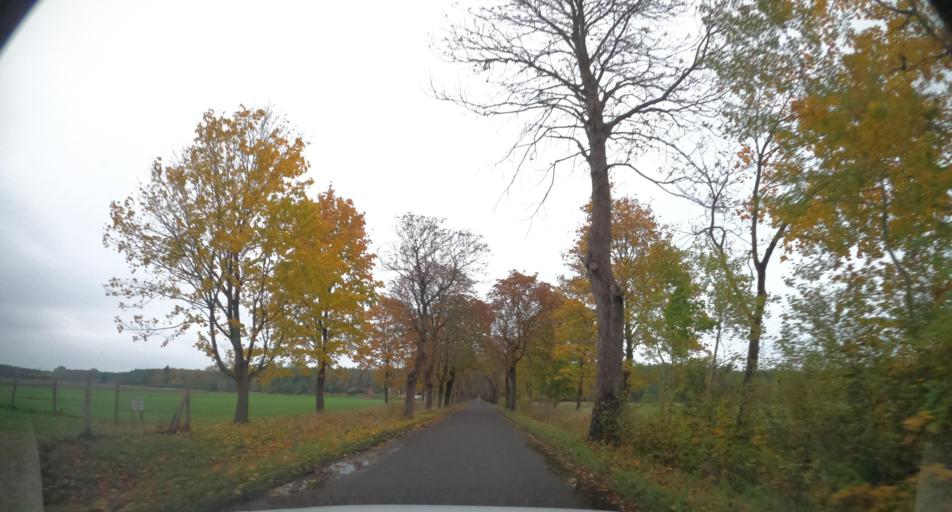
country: PL
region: West Pomeranian Voivodeship
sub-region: Powiat kamienski
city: Wolin
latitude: 53.9339
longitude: 14.6093
